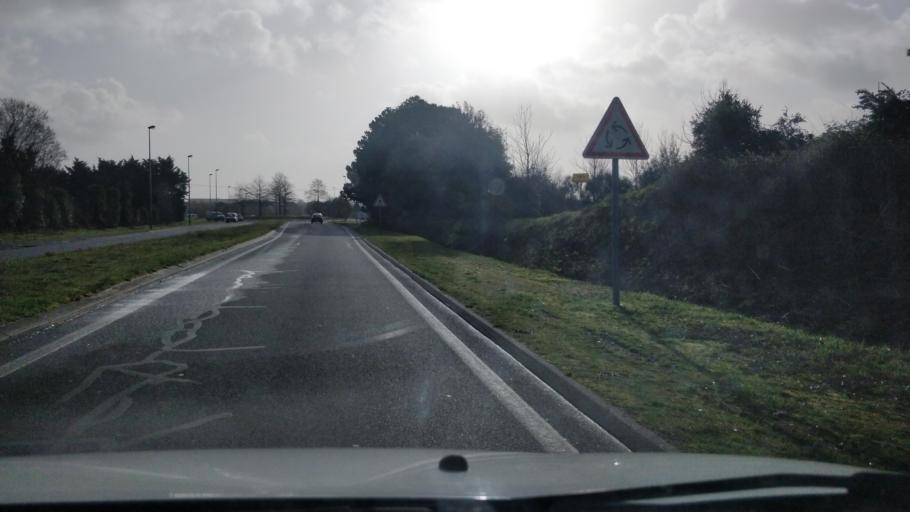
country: FR
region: Pays de la Loire
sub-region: Departement de la Loire-Atlantique
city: Guerande
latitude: 47.3348
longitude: -2.4210
